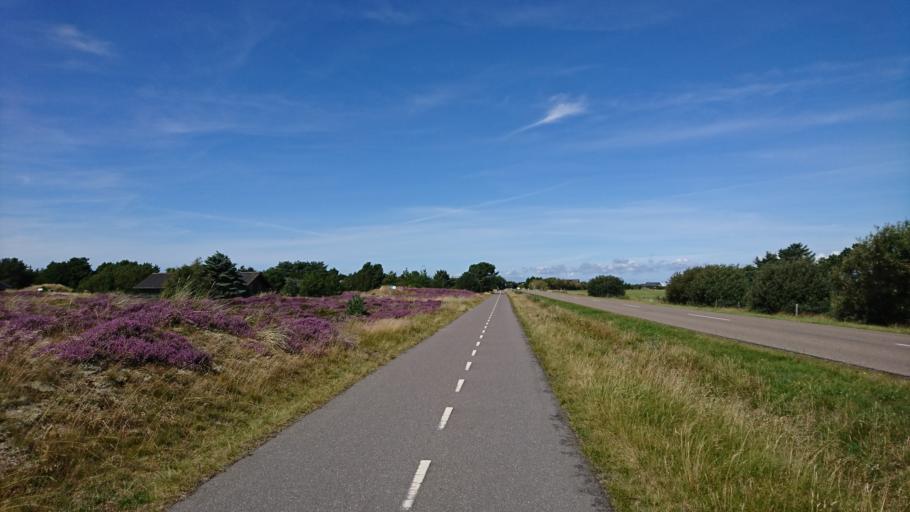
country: DK
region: South Denmark
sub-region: Fano Kommune
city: Nordby
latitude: 55.4152
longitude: 8.4035
